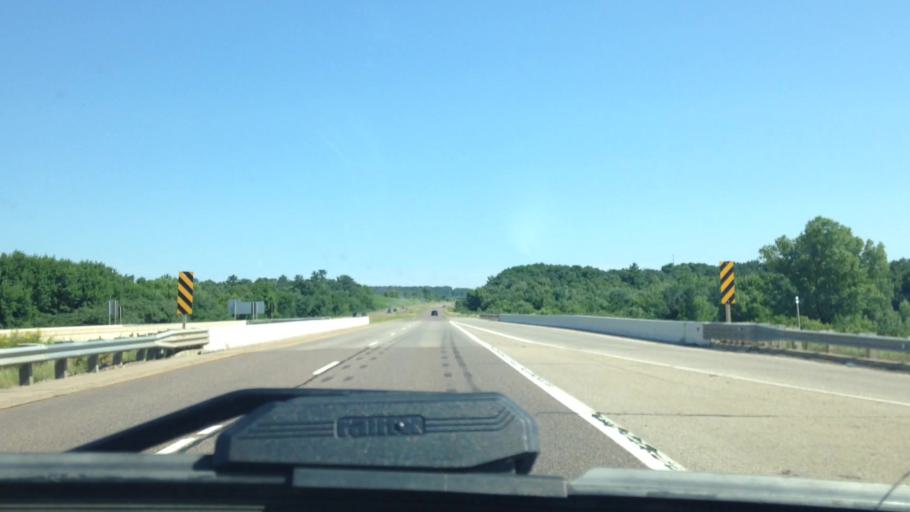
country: US
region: Wisconsin
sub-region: Chippewa County
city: Chippewa Falls
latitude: 44.9262
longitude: -91.4281
